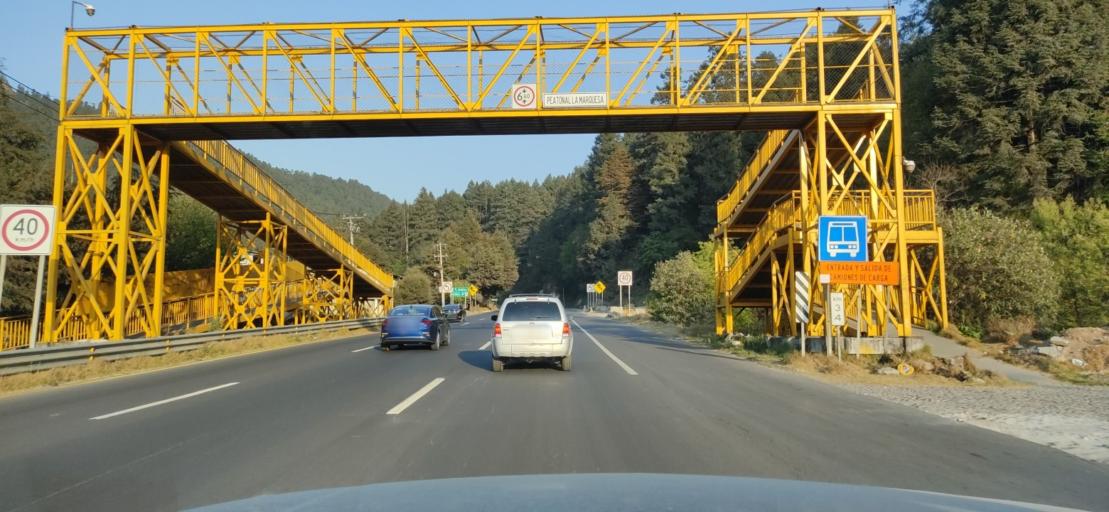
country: MX
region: Mexico City
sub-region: Cuajimalpa de Morelos
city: San Lorenzo Acopilco
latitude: 19.2976
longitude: -99.3690
